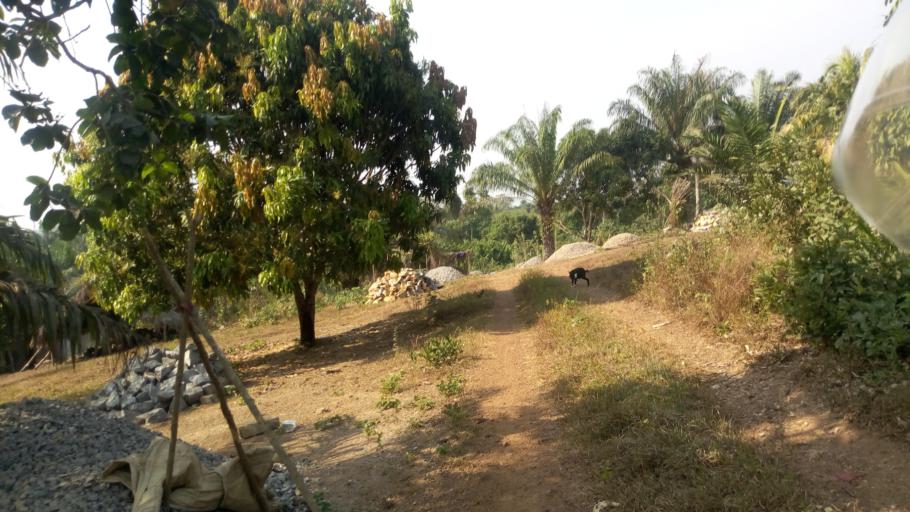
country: SL
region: Southern Province
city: Mogbwemo
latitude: 7.6162
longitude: -12.1826
